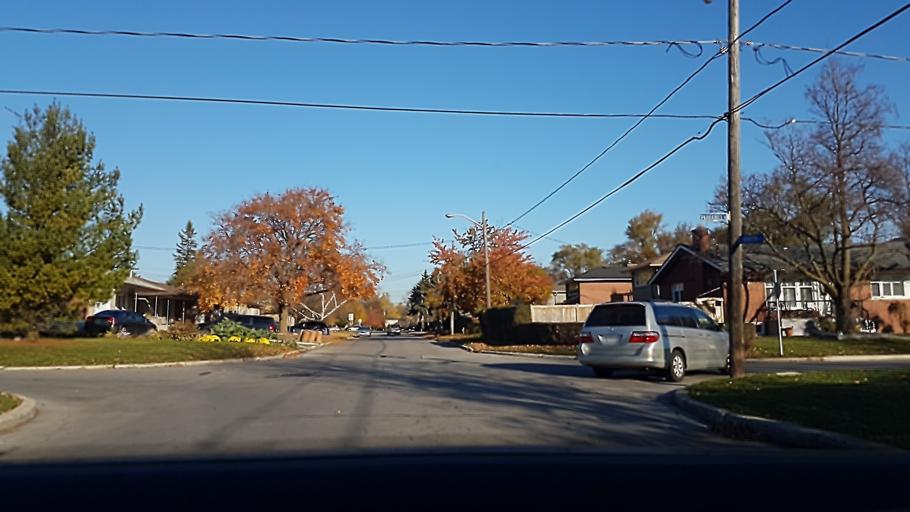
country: CA
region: Ontario
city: Concord
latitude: 43.7607
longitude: -79.4610
